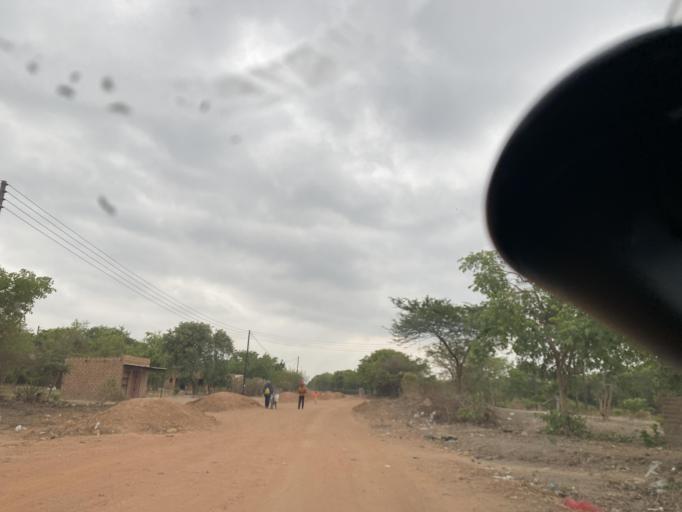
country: ZM
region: Lusaka
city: Chongwe
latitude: -15.2808
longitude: 28.7297
